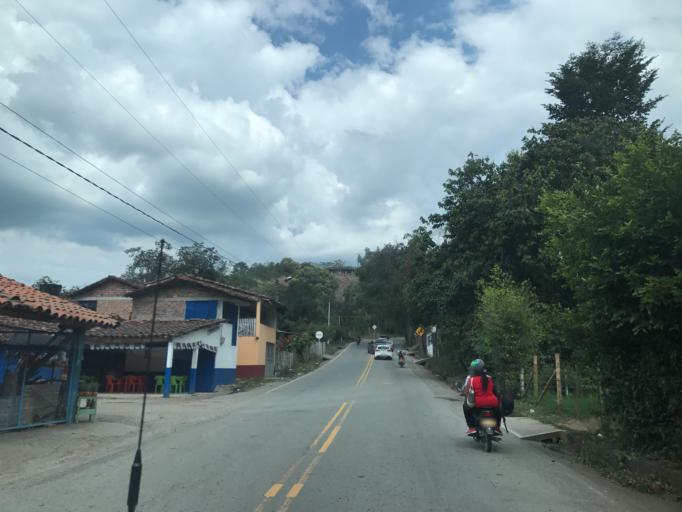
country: CO
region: Valle del Cauca
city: Cartago
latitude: 4.7090
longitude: -75.8565
